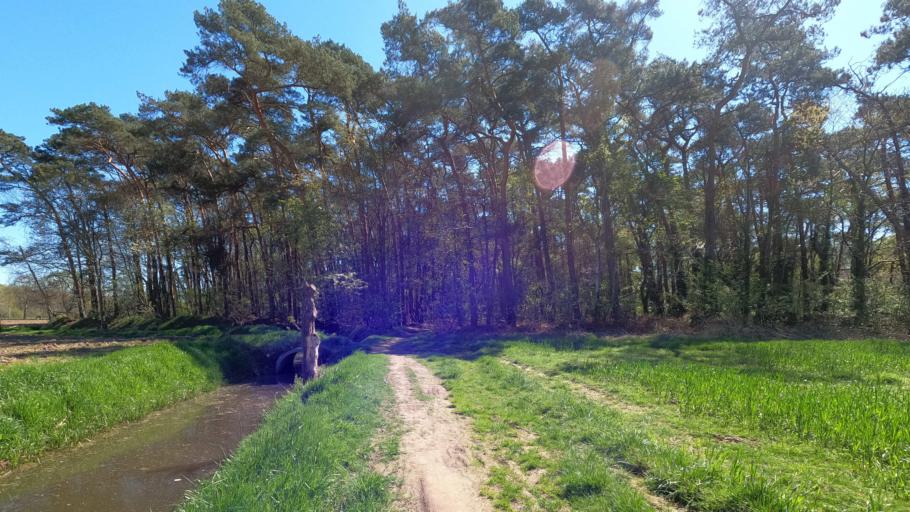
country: BE
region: Flanders
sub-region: Provincie Vlaams-Brabant
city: Haacht
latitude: 50.9787
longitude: 4.6525
